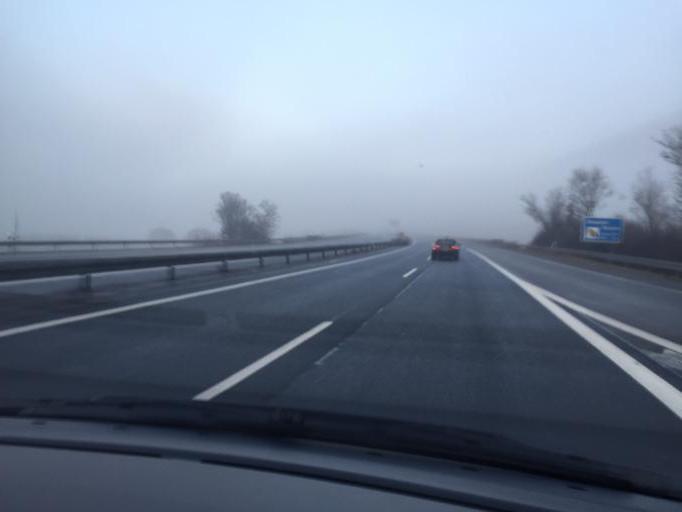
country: DE
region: Baden-Wuerttemberg
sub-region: Freiburg Region
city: Geisingen
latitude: 47.9208
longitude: 8.6738
